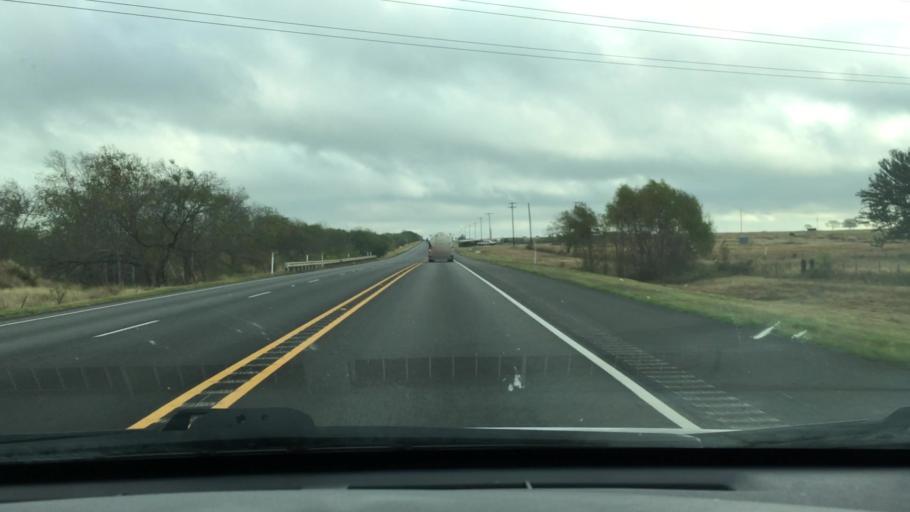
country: US
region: Texas
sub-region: Gonzales County
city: Nixon
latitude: 29.2581
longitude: -97.8053
